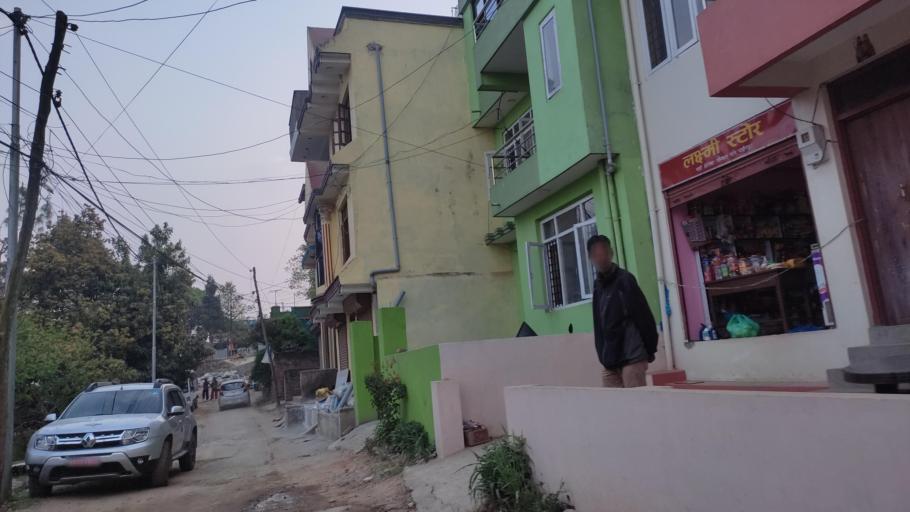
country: NP
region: Central Region
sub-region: Bagmati Zone
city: Patan
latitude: 27.6652
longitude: 85.2937
